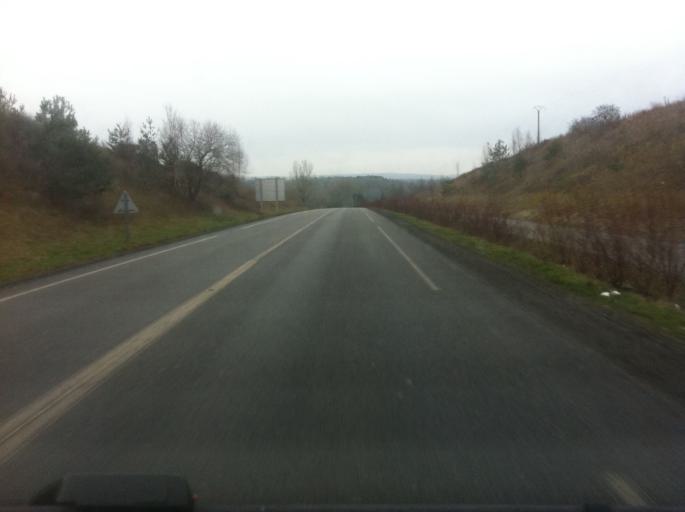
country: FR
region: Haute-Normandie
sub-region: Departement de la Seine-Maritime
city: La Mailleraye-sur-Seine
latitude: 49.4749
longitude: 0.7626
